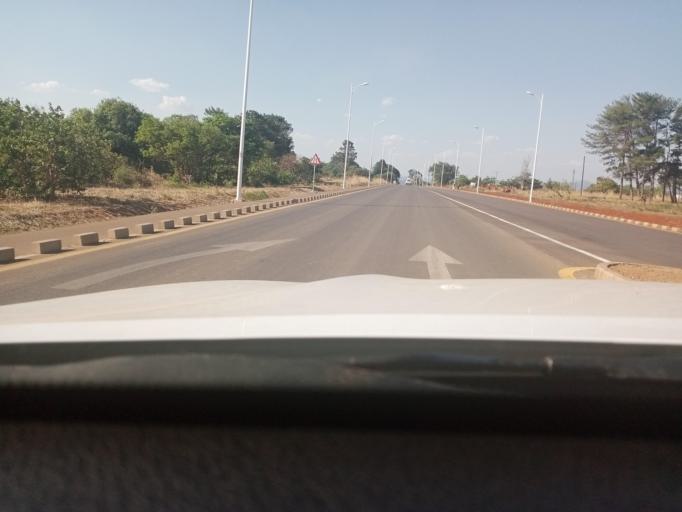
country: ZM
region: Northern
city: Mpika
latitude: -11.8132
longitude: 31.4509
